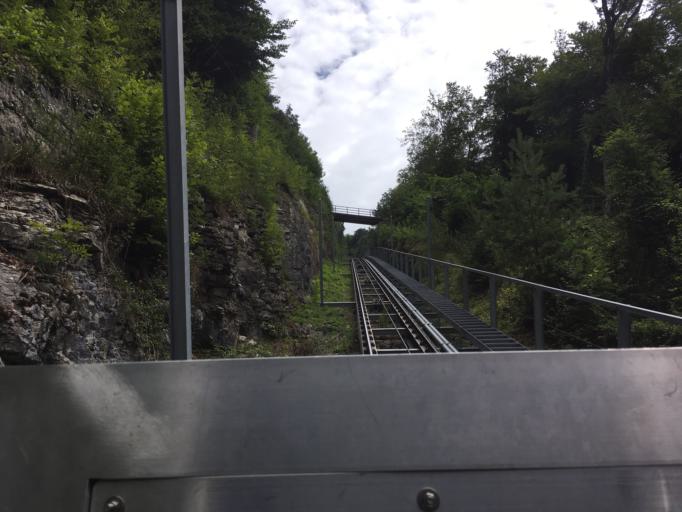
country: CH
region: Bern
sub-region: Thun District
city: Sigriswil
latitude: 46.6855
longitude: 7.7488
